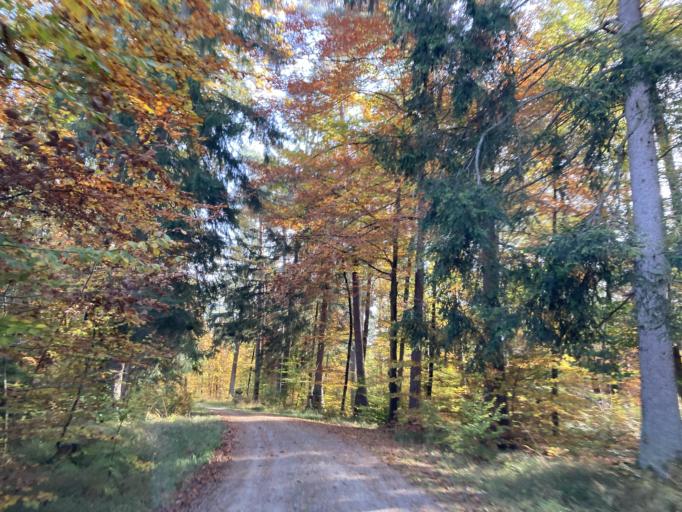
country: DE
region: Baden-Wuerttemberg
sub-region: Tuebingen Region
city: Bodelshausen
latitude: 48.4186
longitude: 8.9464
